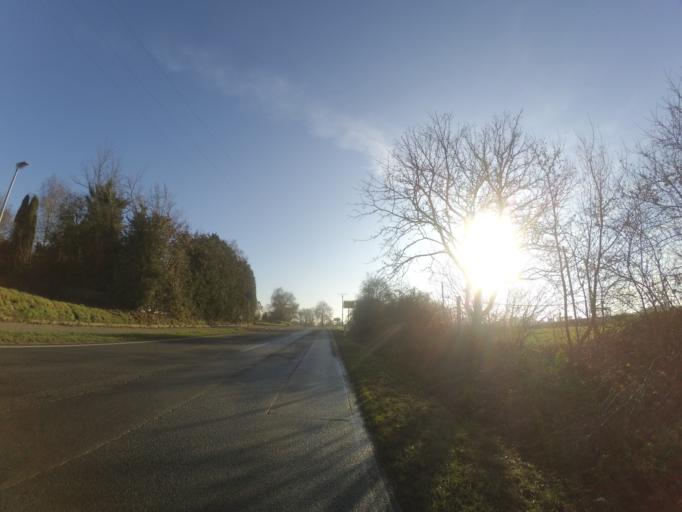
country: DE
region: Baden-Wuerttemberg
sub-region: Tuebingen Region
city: Dornstadt
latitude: 48.4592
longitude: 9.9078
